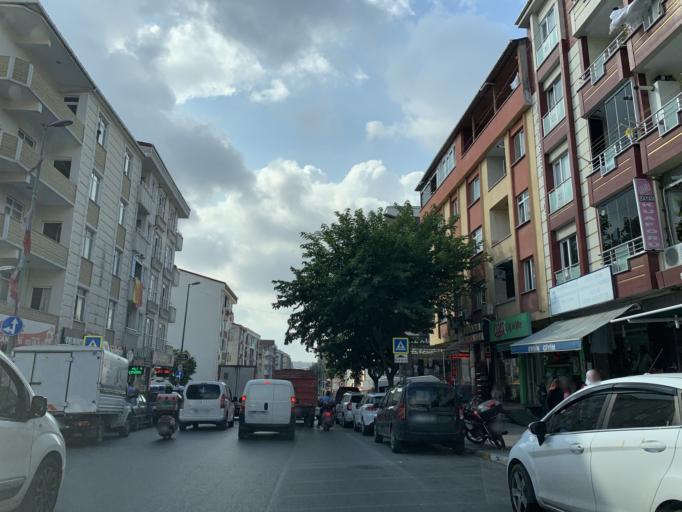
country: TR
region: Istanbul
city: Esenyurt
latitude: 41.0220
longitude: 28.6734
